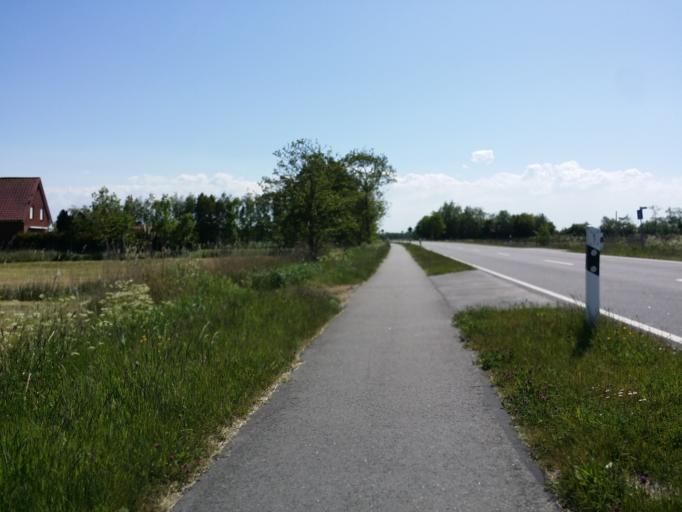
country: DE
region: Lower Saxony
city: Esens
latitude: 53.6630
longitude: 7.6138
